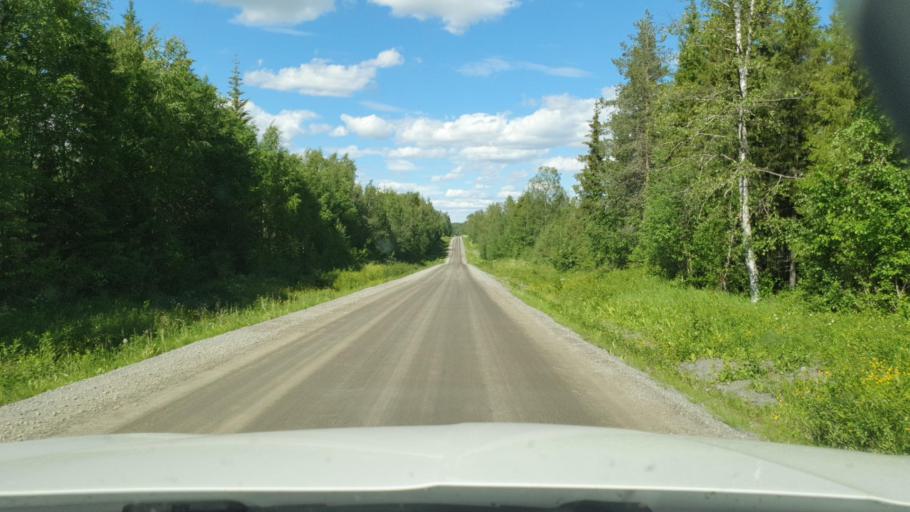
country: SE
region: Vaesterbotten
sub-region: Skelleftea Kommun
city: Forsbacka
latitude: 64.7782
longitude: 20.5154
